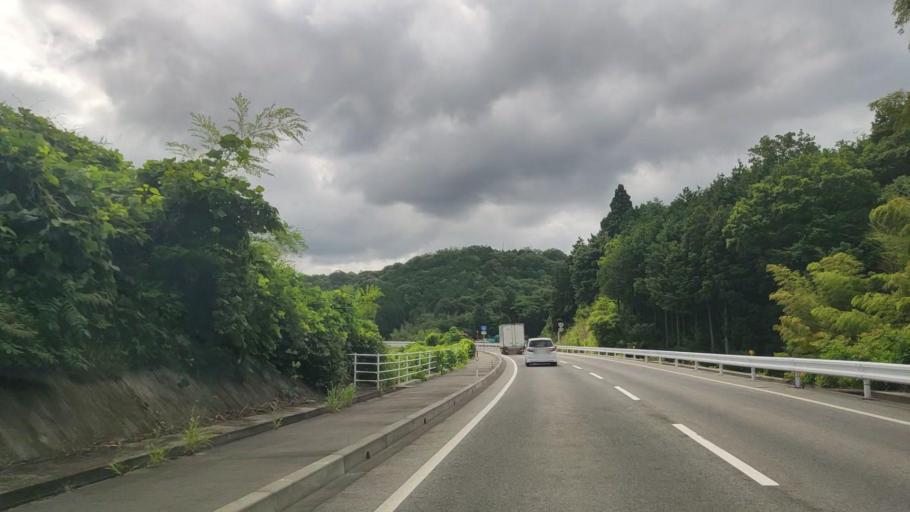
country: JP
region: Tottori
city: Yonago
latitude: 35.3770
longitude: 133.3952
